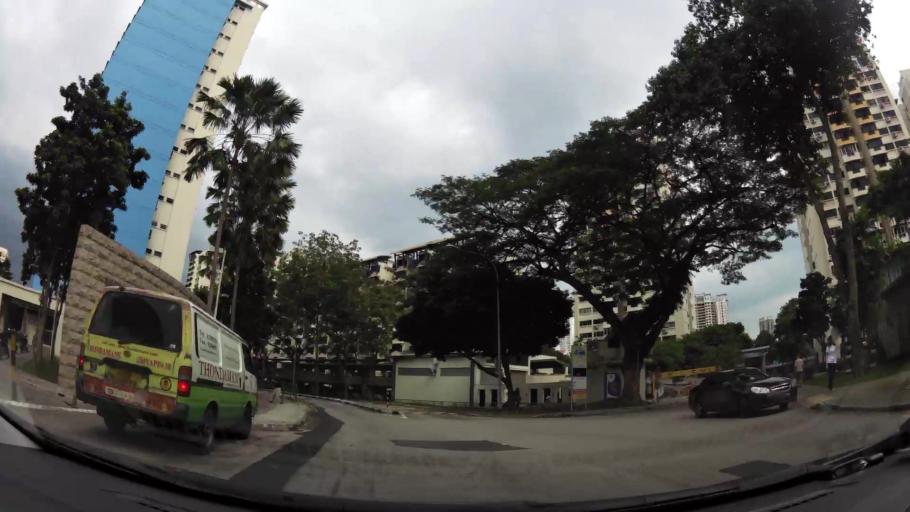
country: SG
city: Singapore
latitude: 1.3226
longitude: 103.8554
